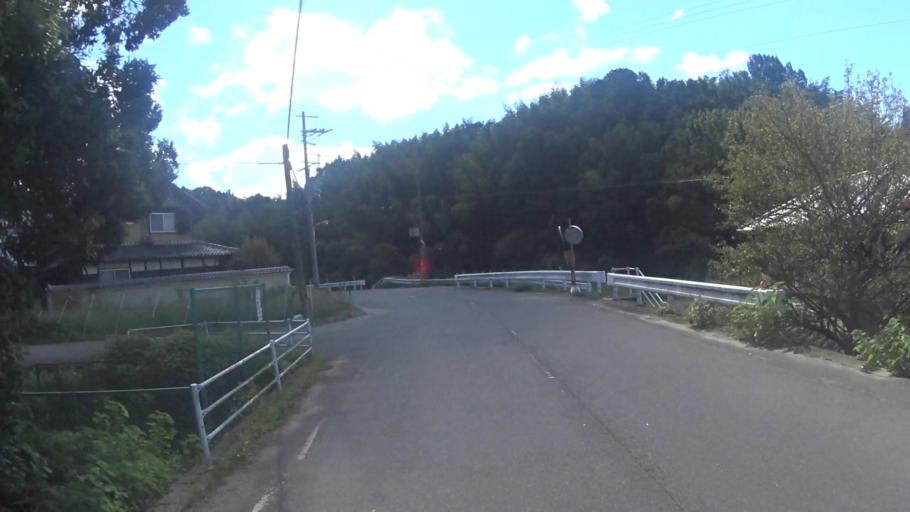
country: JP
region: Nara
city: Nara-shi
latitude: 34.7317
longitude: 135.8844
